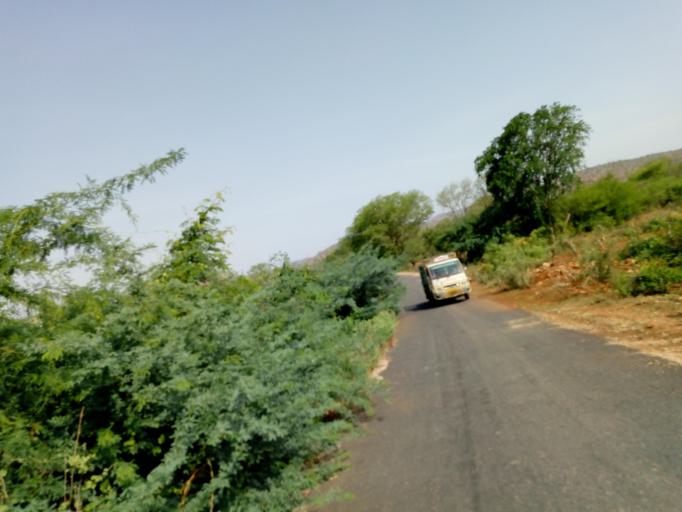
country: IN
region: Andhra Pradesh
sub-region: Prakasam
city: Cumbum
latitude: 15.7148
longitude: 79.0795
